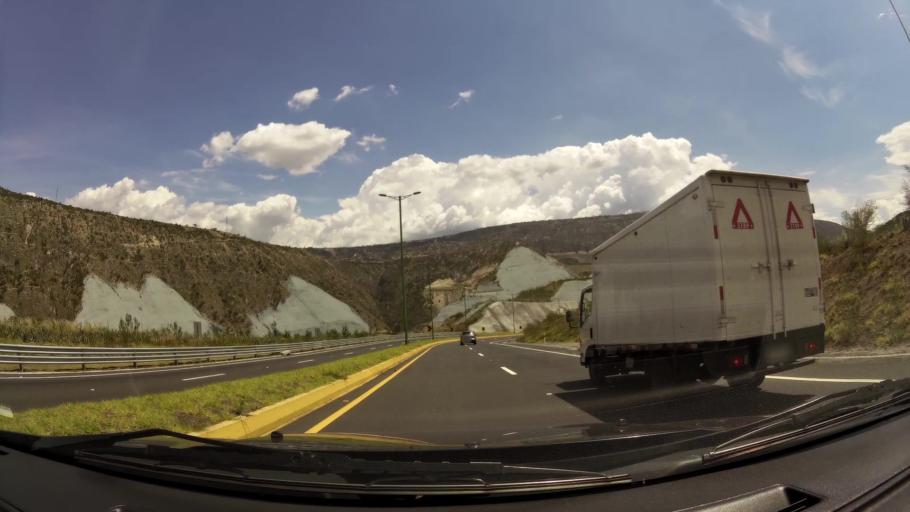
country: EC
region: Pichincha
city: Quito
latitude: -0.1037
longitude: -78.3804
